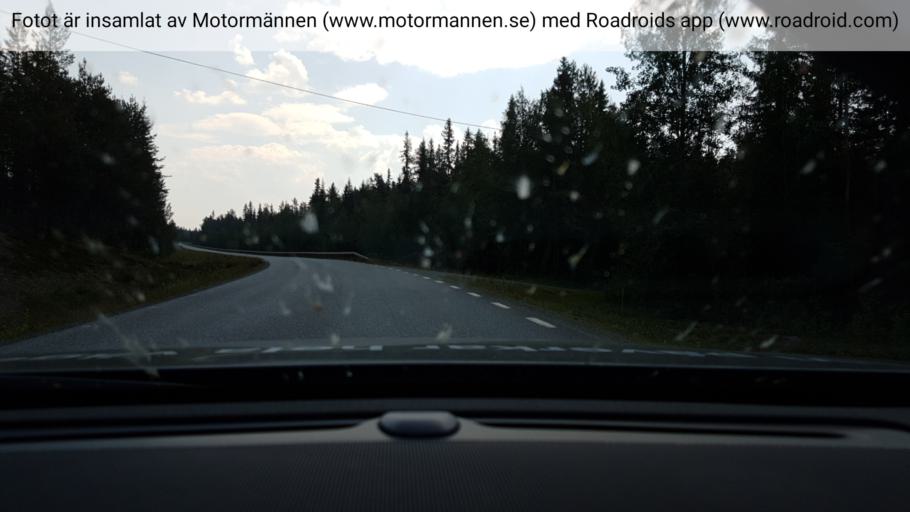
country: SE
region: Vaesterbotten
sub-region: Storumans Kommun
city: Fristad
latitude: 65.4246
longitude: 16.2792
